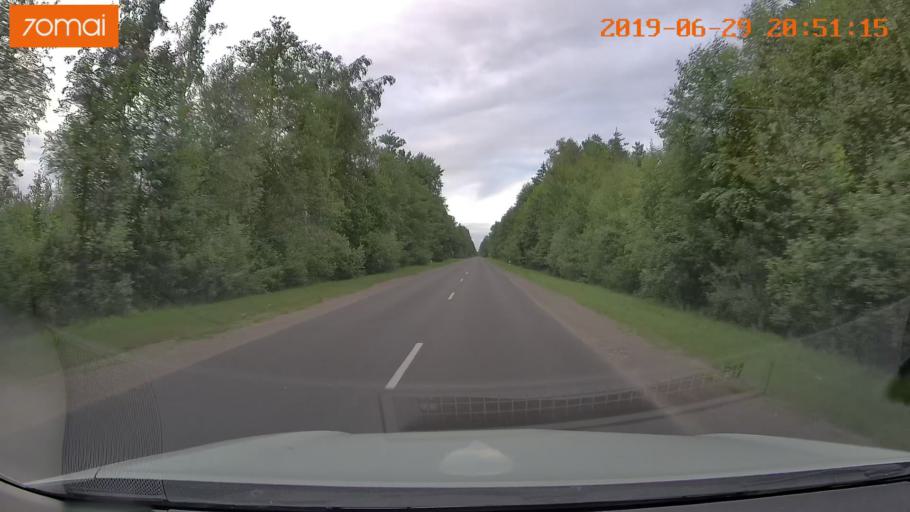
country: BY
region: Brest
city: Hantsavichy
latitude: 52.6858
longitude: 26.3469
